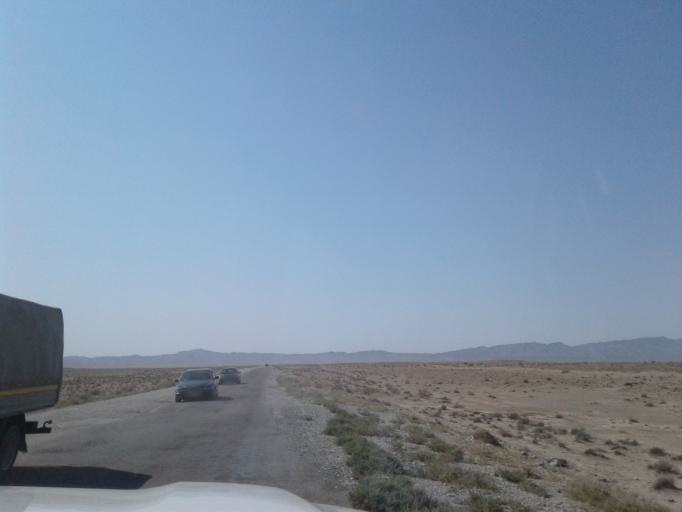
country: TM
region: Balkan
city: Gazanjyk
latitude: 39.2336
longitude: 55.3034
